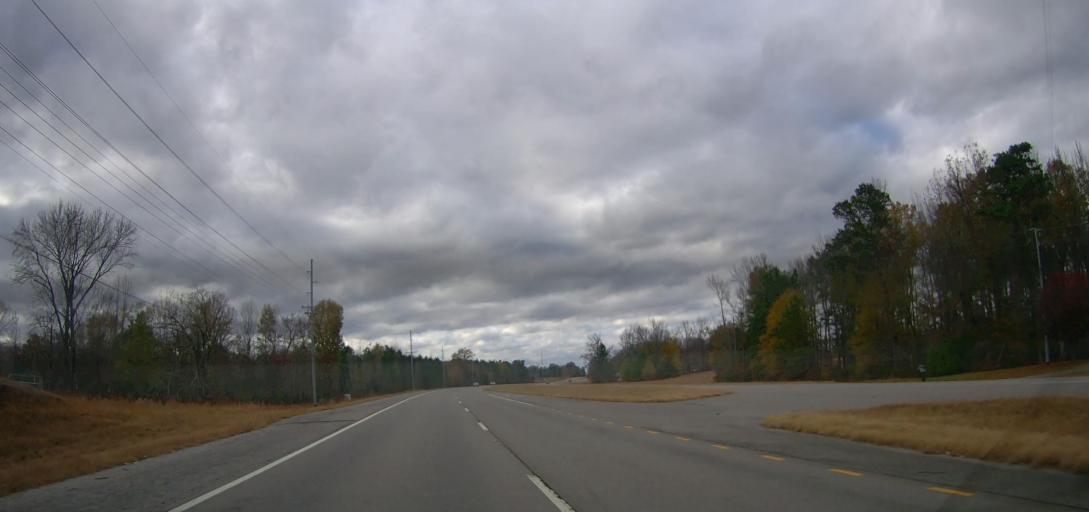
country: US
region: Alabama
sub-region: Lawrence County
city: Town Creek
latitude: 34.5737
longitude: -87.3968
